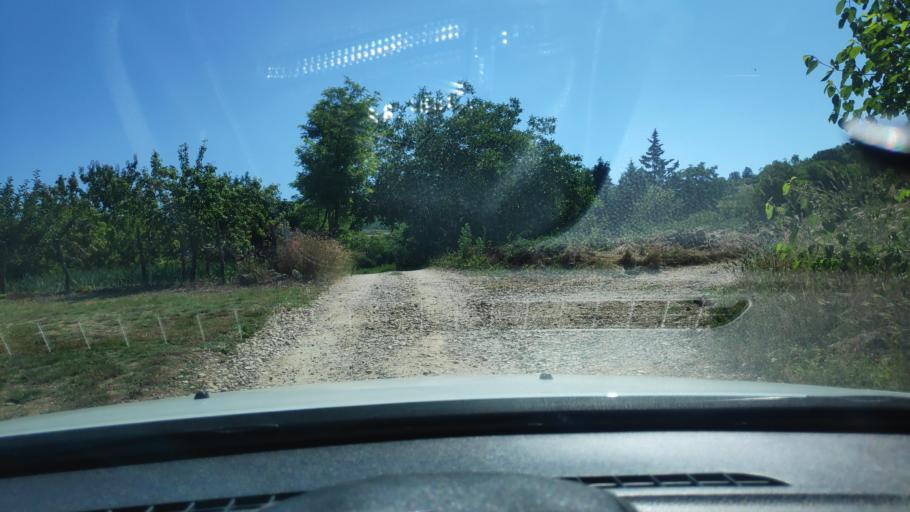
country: MK
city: Klechovce
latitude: 42.0696
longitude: 21.8727
